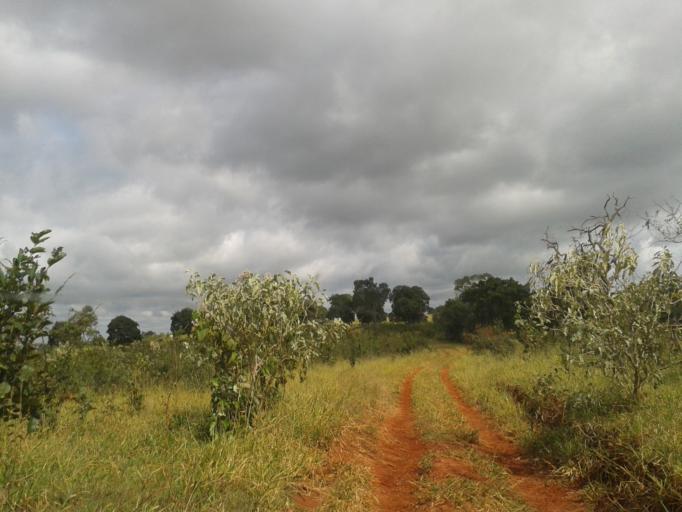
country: BR
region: Minas Gerais
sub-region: Campina Verde
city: Campina Verde
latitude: -19.4131
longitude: -49.6712
